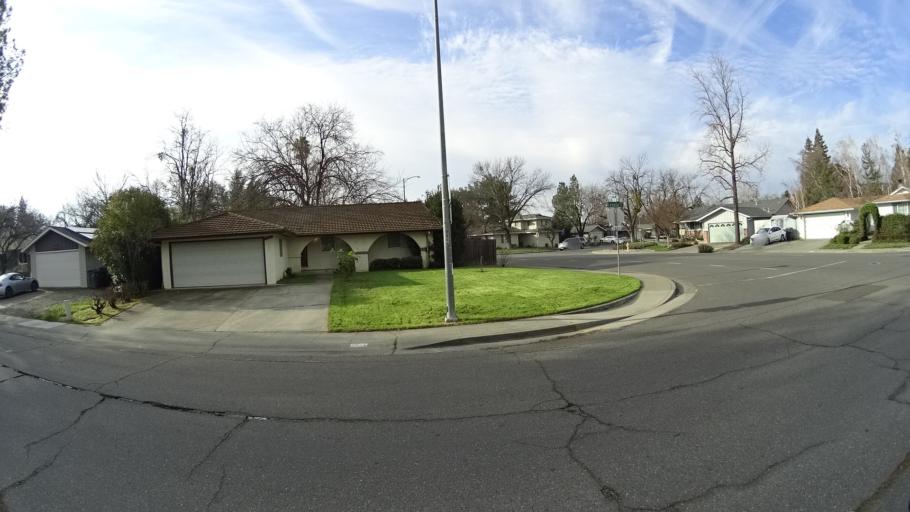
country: US
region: California
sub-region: Yolo County
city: Davis
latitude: 38.5576
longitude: -121.7172
